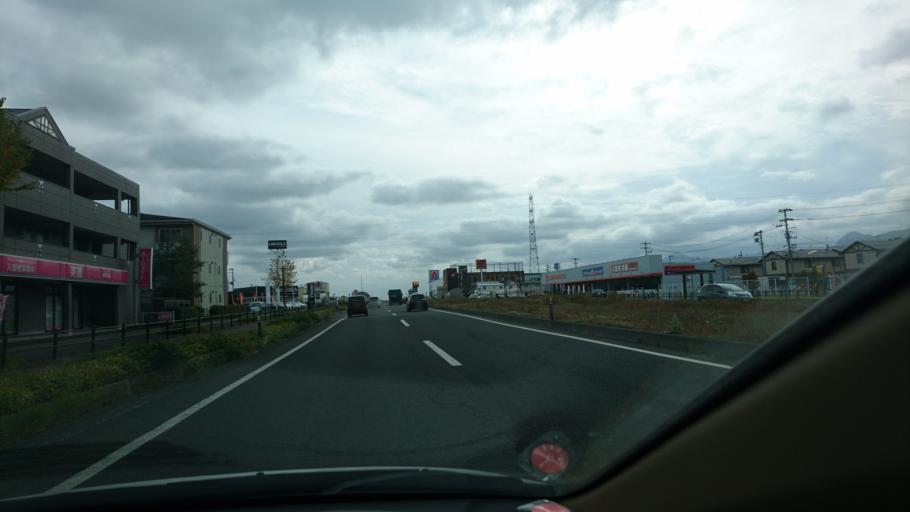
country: JP
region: Iwate
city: Morioka-shi
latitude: 39.6826
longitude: 141.1356
